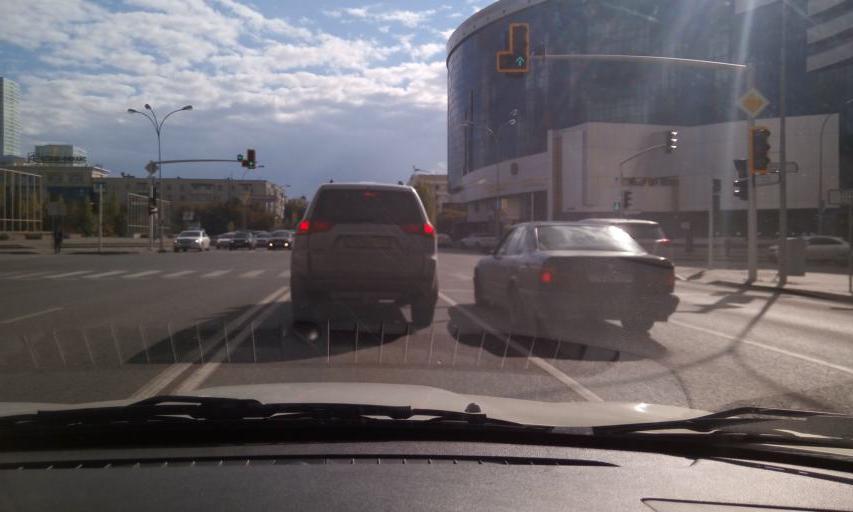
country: KZ
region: Astana Qalasy
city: Astana
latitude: 51.1670
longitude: 71.4136
